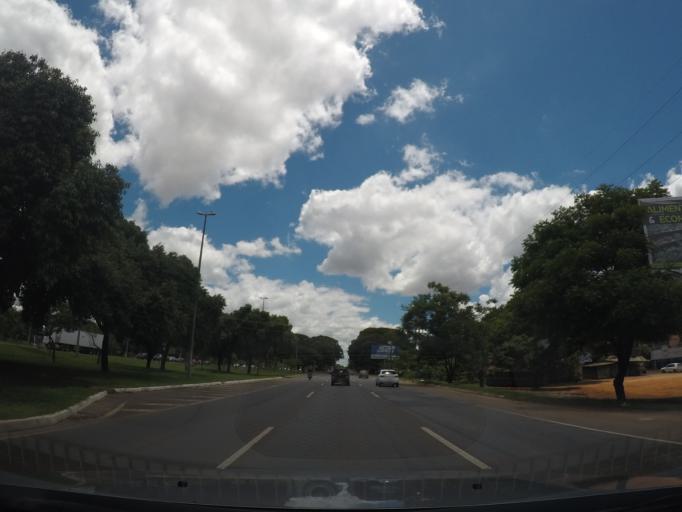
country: BR
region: Federal District
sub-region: Brasilia
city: Brasilia
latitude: -15.7987
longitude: -47.9460
